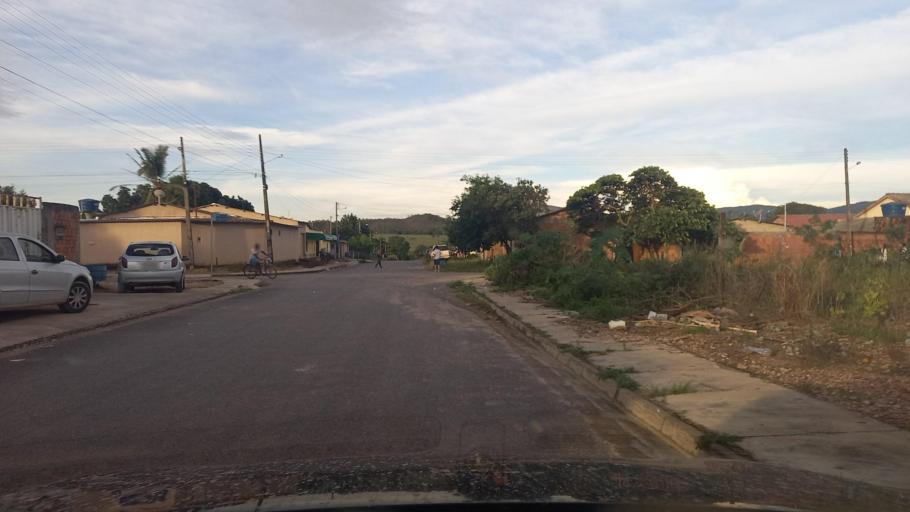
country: BR
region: Goias
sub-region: Cavalcante
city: Cavalcante
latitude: -13.7915
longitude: -47.4551
